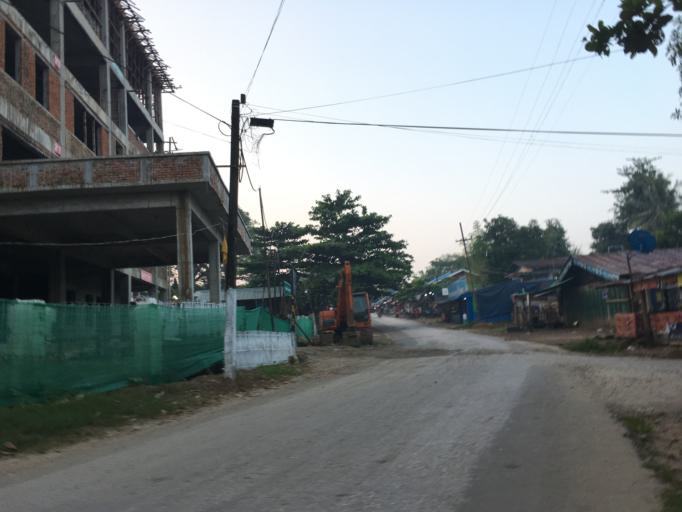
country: MM
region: Mon
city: Mawlamyine
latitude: 16.4819
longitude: 97.6264
